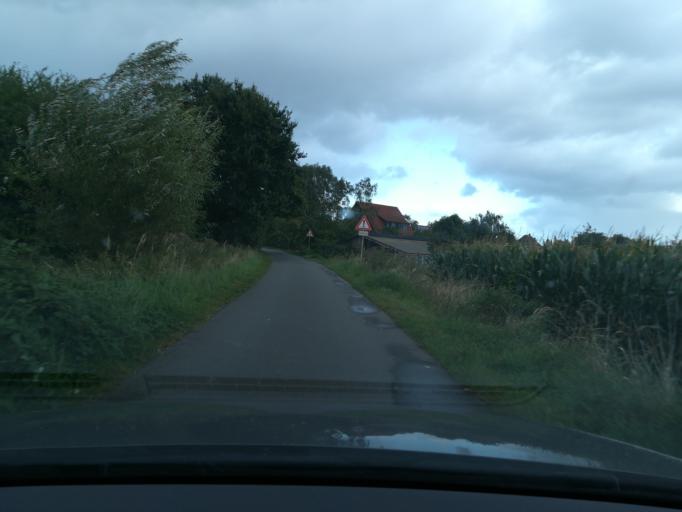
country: DE
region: Lower Saxony
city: Drage
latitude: 53.4229
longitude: 10.2511
